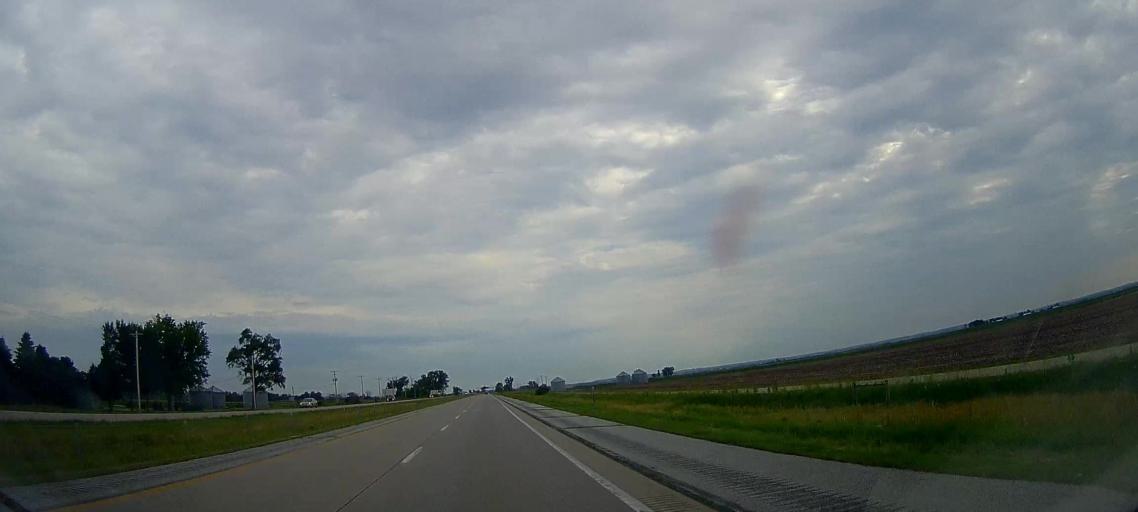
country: US
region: Iowa
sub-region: Harrison County
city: Missouri Valley
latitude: 41.5321
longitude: -95.9179
